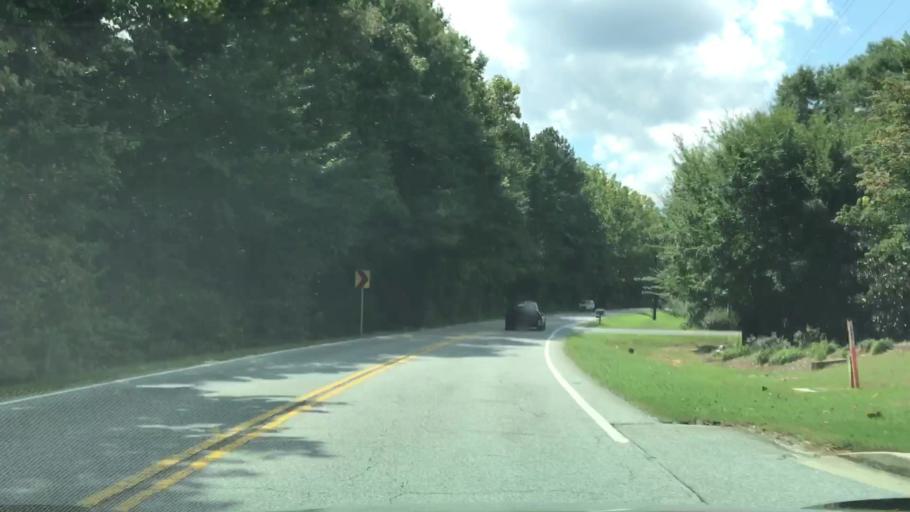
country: US
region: Georgia
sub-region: Gwinnett County
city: Snellville
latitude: 33.9165
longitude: -84.0612
